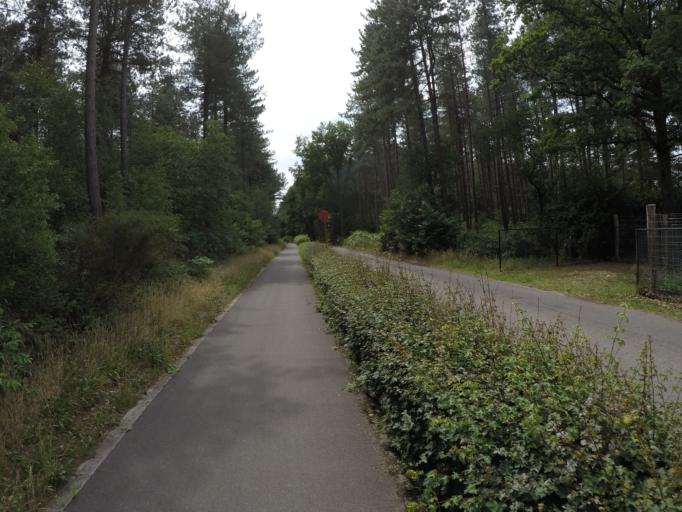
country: BE
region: Flanders
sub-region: Provincie Antwerpen
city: Essen
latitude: 51.4737
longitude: 4.5293
